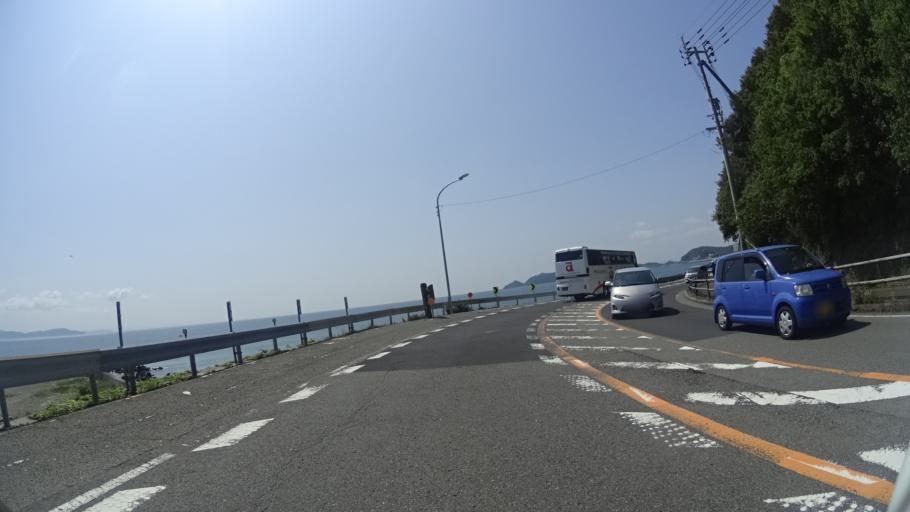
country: JP
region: Tokushima
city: Narutocho-mitsuishi
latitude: 34.2140
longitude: 134.6299
